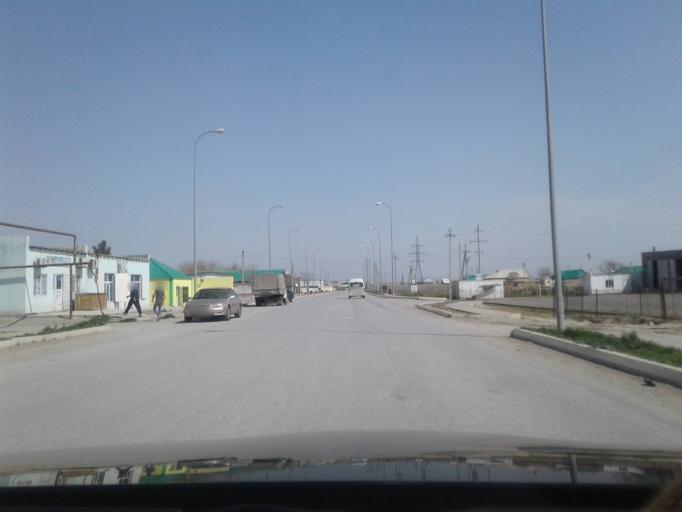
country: TM
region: Ahal
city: Abadan
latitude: 38.1590
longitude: 57.9763
